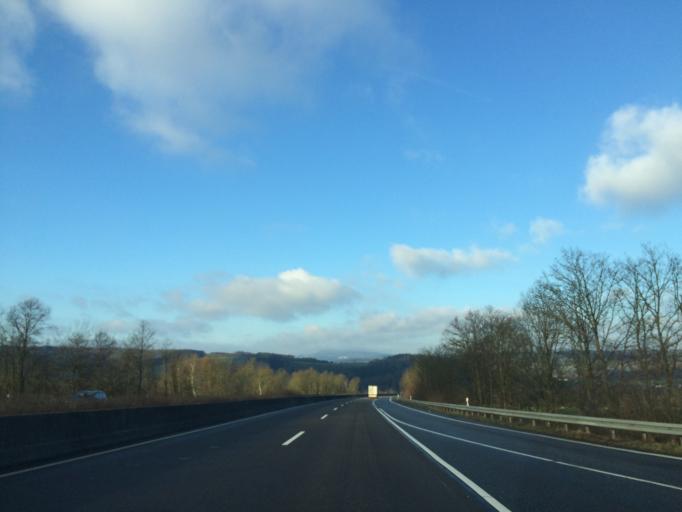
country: DE
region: Hesse
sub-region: Regierungsbezirk Kassel
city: Niederaula
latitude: 50.7612
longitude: 9.6000
